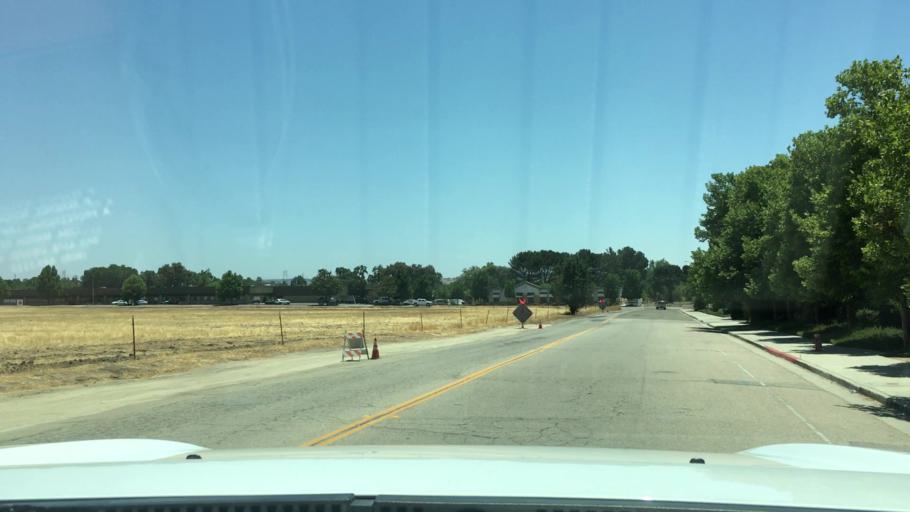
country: US
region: California
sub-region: San Luis Obispo County
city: Paso Robles
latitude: 35.6153
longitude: -120.6502
